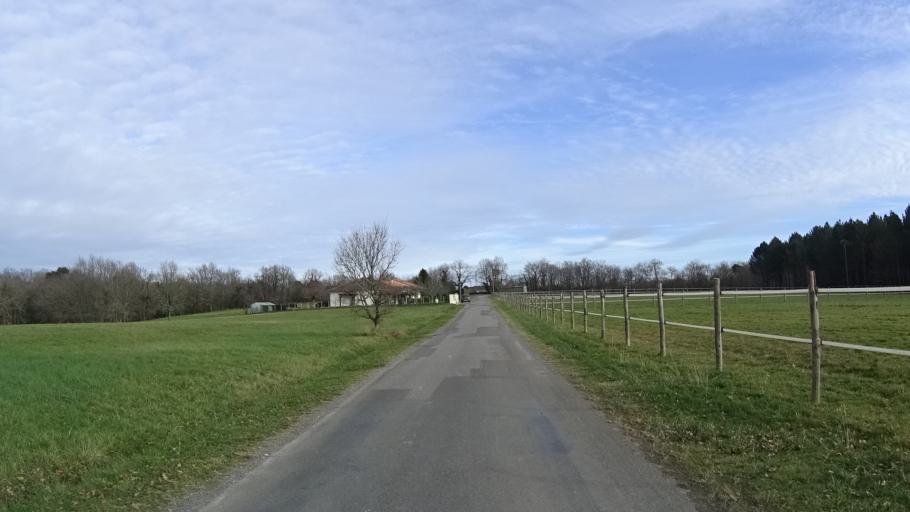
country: FR
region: Aquitaine
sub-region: Departement de la Dordogne
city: Riberac
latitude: 45.1978
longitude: 0.3619
